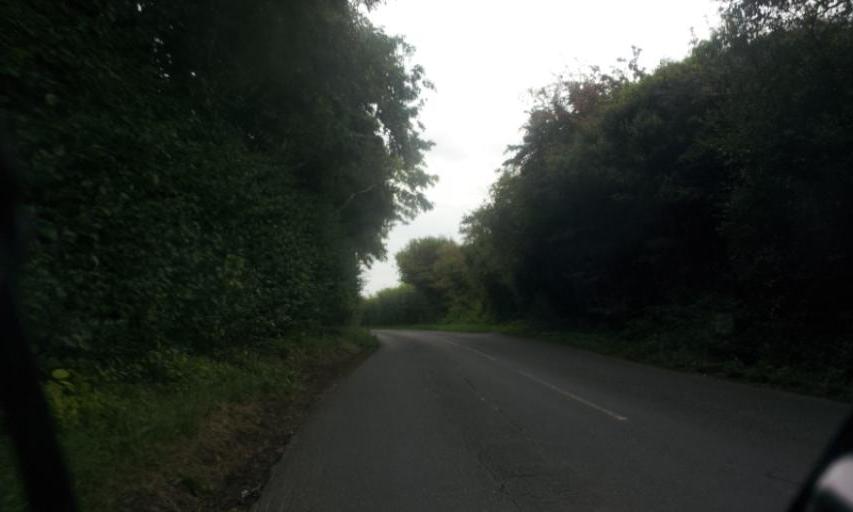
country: GB
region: England
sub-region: Kent
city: Hadlow
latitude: 51.2088
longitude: 0.3593
